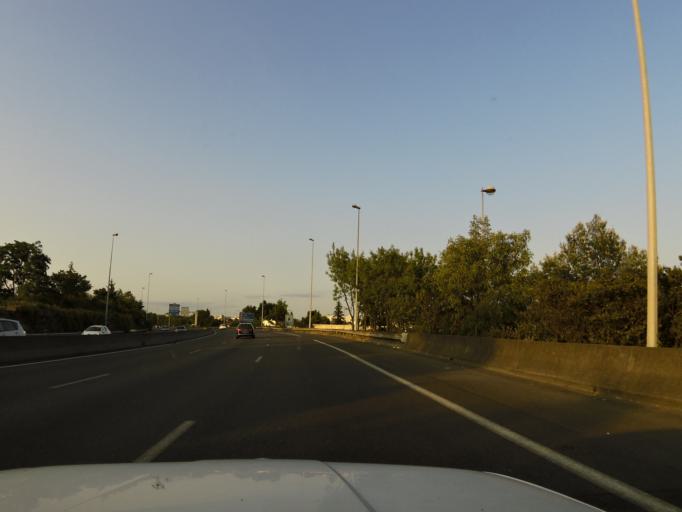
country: FR
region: Rhone-Alpes
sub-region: Departement du Rhone
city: Villeurbanne
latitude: 45.7840
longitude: 4.8951
